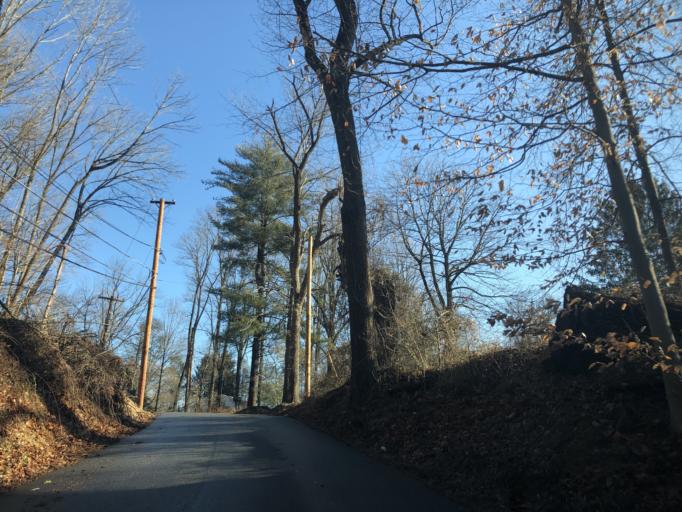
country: US
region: Pennsylvania
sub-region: Delaware County
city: Chester Heights
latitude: 39.9329
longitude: -75.4916
